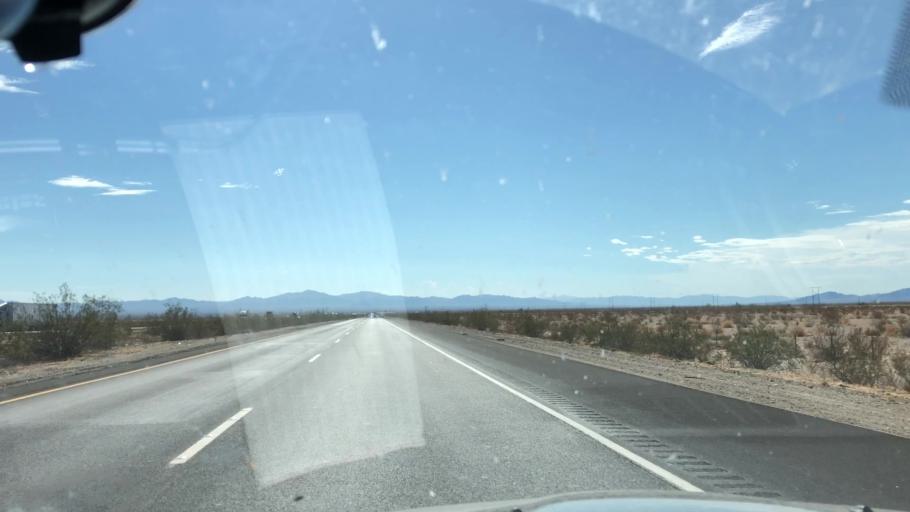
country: US
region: California
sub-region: Riverside County
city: Mesa Verde
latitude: 33.6099
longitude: -114.8457
